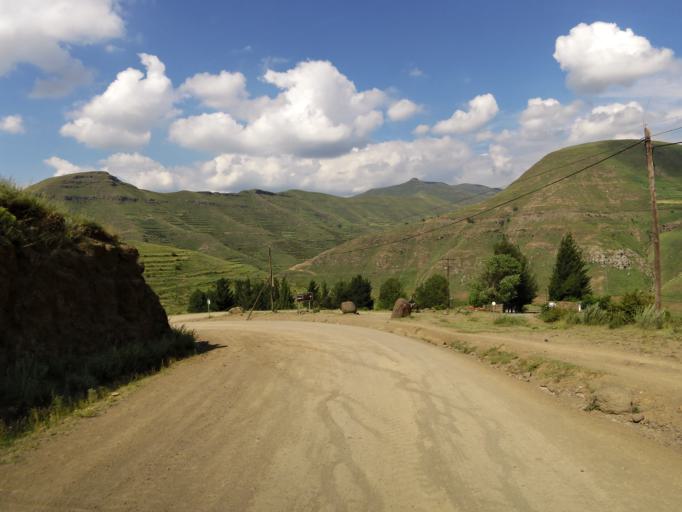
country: LS
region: Butha-Buthe
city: Butha-Buthe
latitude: -29.1045
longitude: 28.5023
